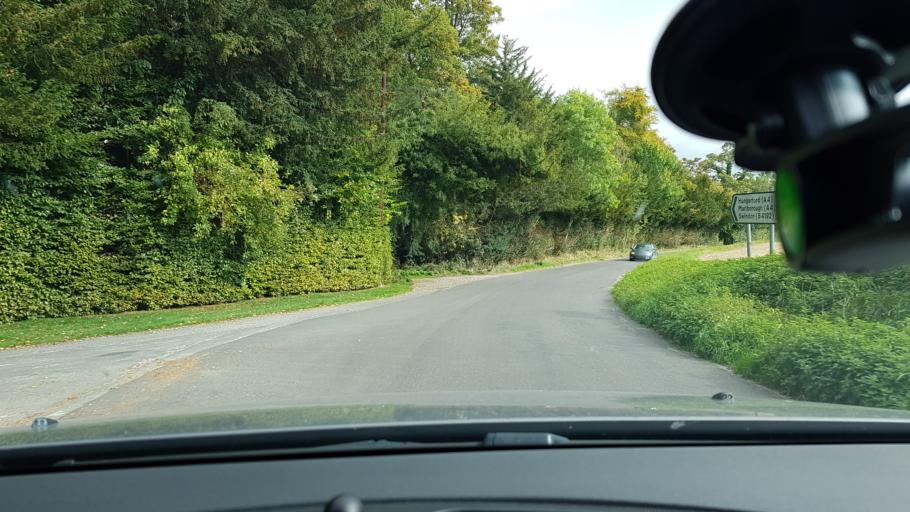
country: GB
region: England
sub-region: Wiltshire
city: Chilton Foliat
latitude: 51.4296
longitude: -1.5536
